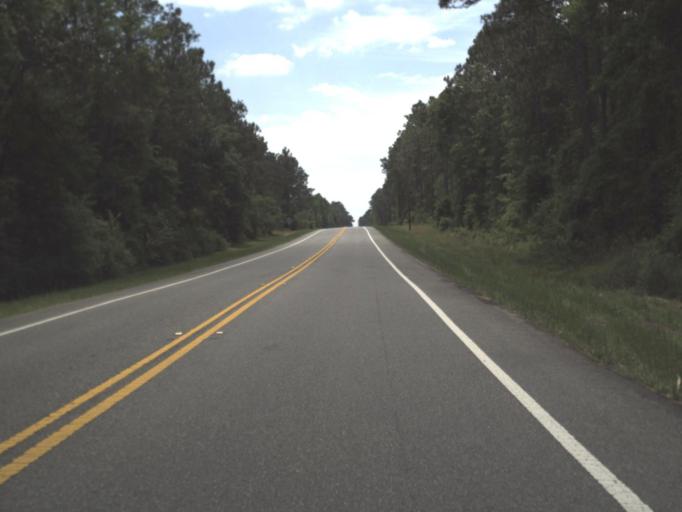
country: US
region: Florida
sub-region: Calhoun County
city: Blountstown
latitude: 30.3798
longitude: -85.0873
